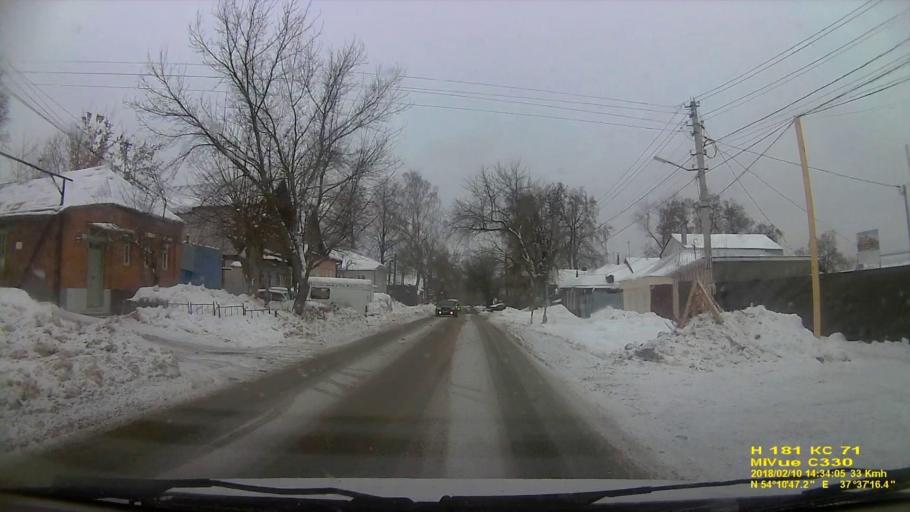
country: RU
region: Tula
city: Tula
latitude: 54.1798
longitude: 37.6212
